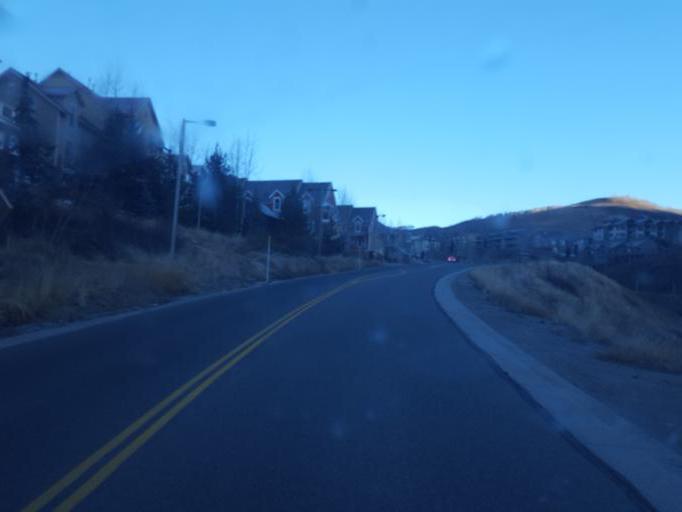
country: US
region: Colorado
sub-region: Gunnison County
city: Crested Butte
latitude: 38.8931
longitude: -106.9711
